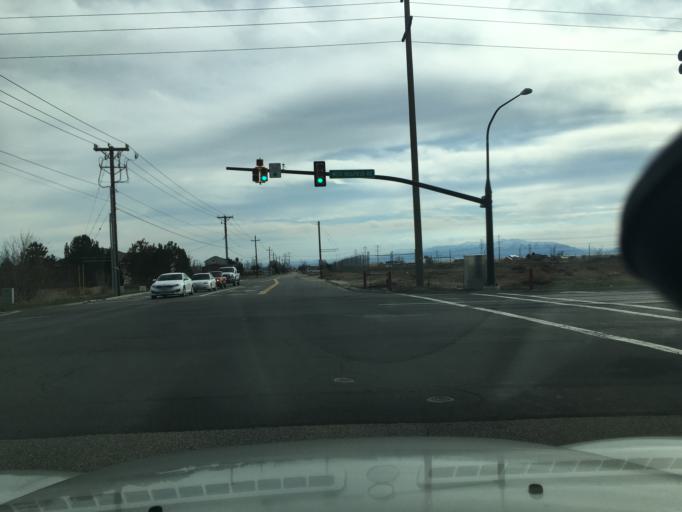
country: US
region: Utah
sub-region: Davis County
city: Layton
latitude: 41.0678
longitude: -112.0071
